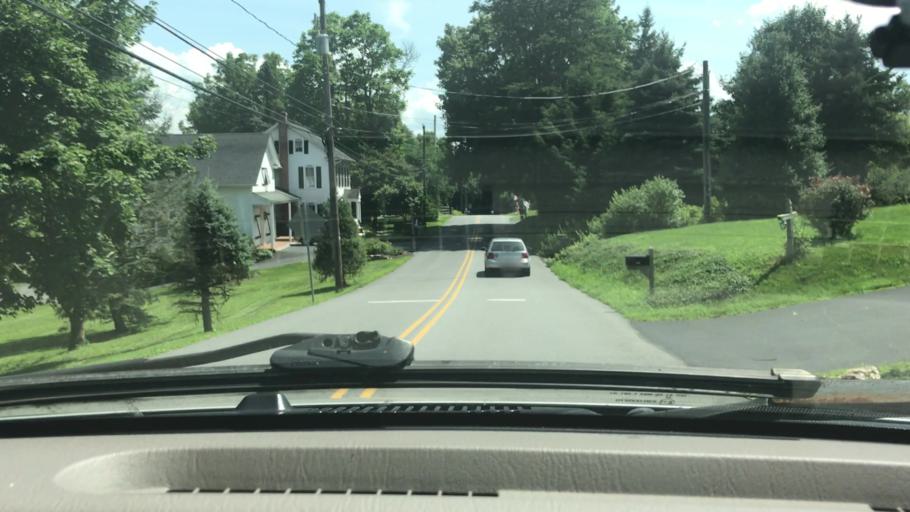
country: US
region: Pennsylvania
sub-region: Dauphin County
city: Rutherford
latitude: 40.2579
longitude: -76.7477
